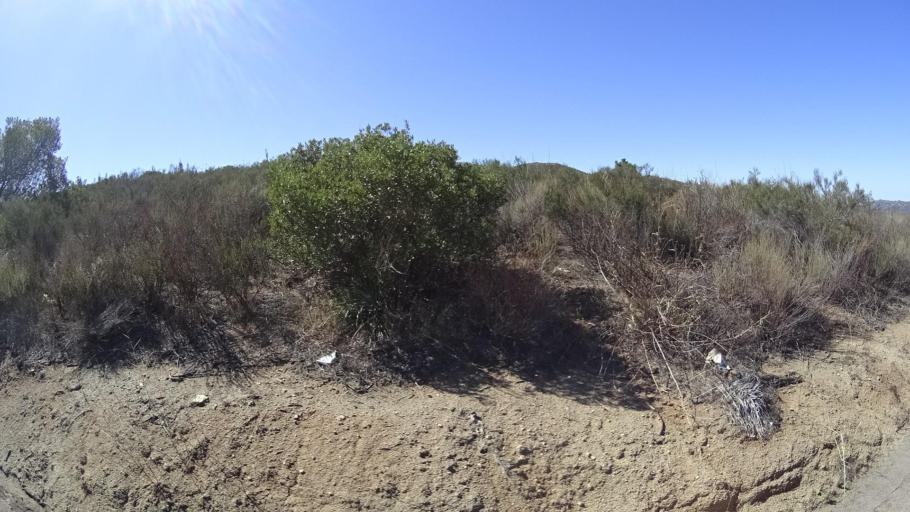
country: US
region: California
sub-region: San Diego County
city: Alpine
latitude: 32.7856
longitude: -116.7216
